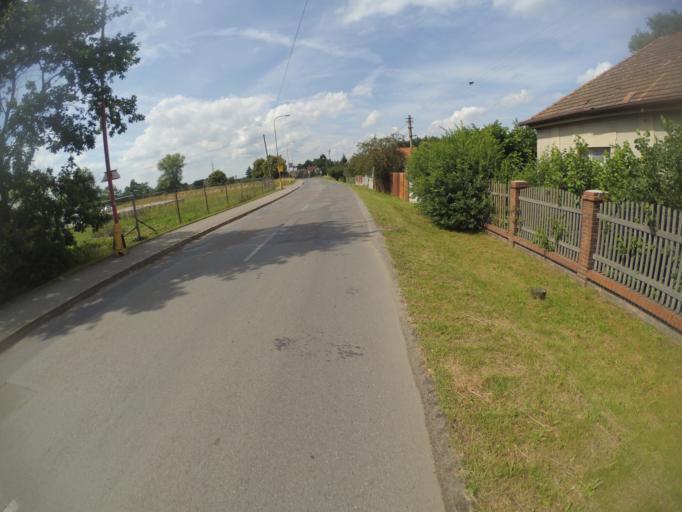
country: CZ
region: Central Bohemia
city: Libis
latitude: 50.2703
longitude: 14.5060
